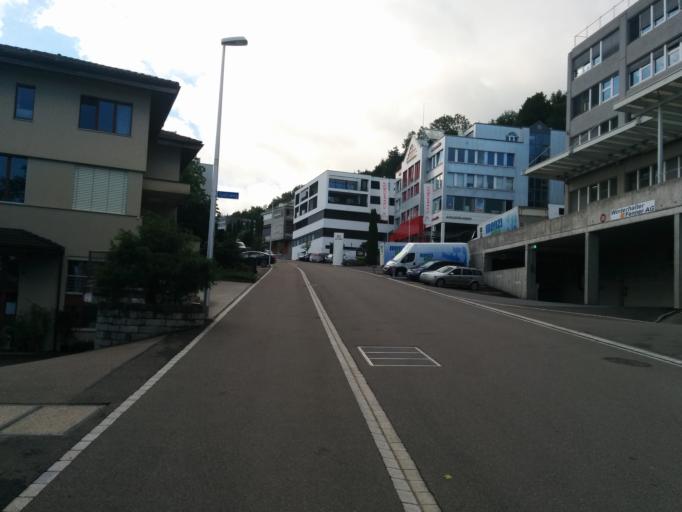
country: CH
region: Zurich
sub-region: Bezirk Horgen
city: Horgen / Scheller-Stockerstrasse
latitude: 47.2603
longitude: 8.5852
